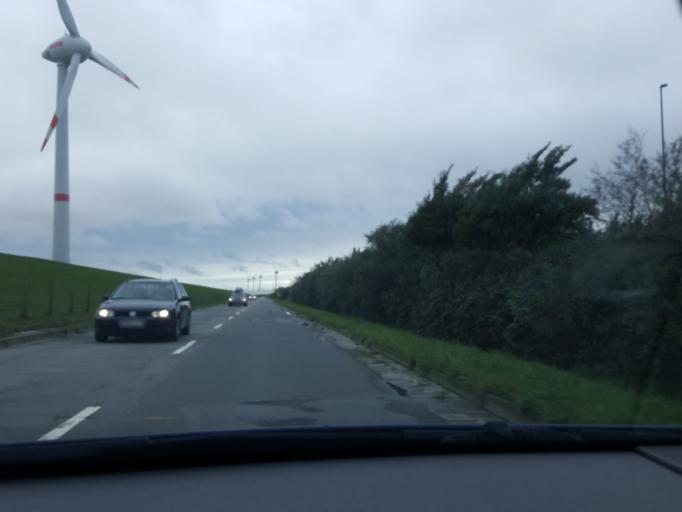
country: DE
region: Lower Saxony
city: Emden
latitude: 53.3333
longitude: 7.2159
